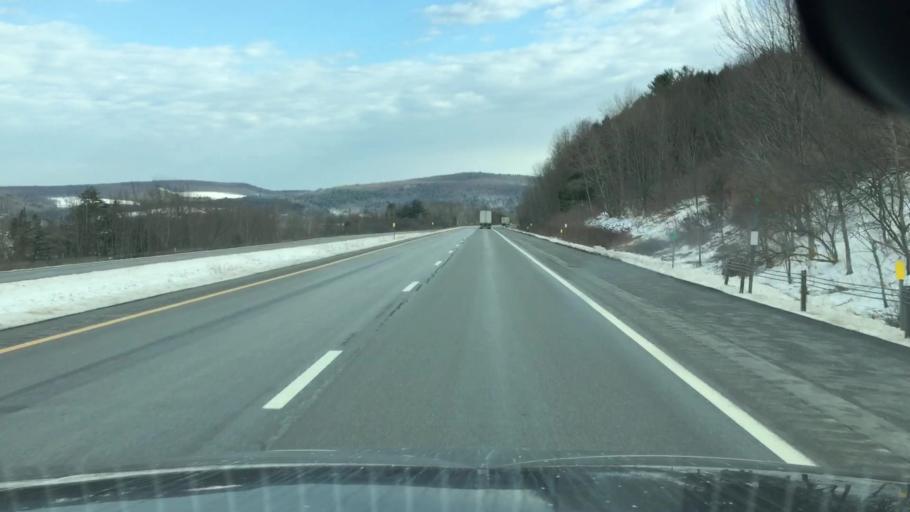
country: US
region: New York
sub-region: Delaware County
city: Sidney
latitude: 42.3018
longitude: -75.3794
